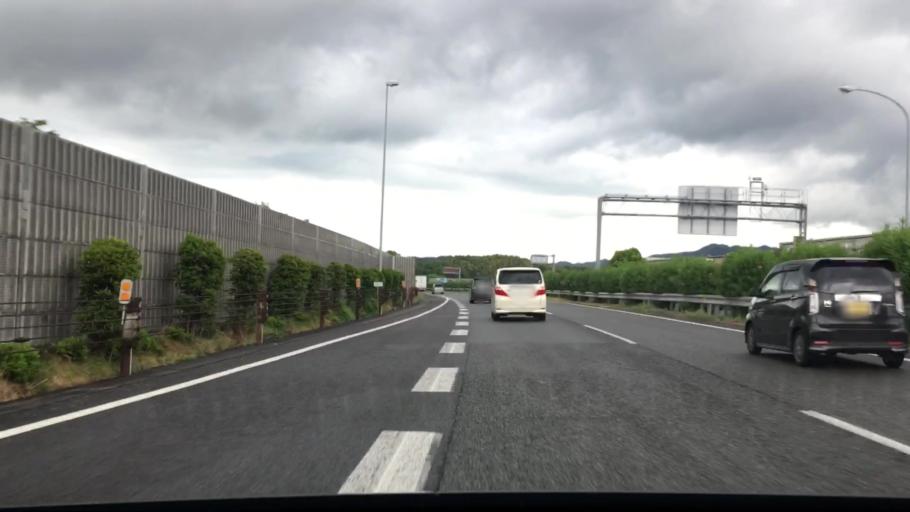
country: JP
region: Fukuoka
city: Sasaguri
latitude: 33.6330
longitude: 130.4906
